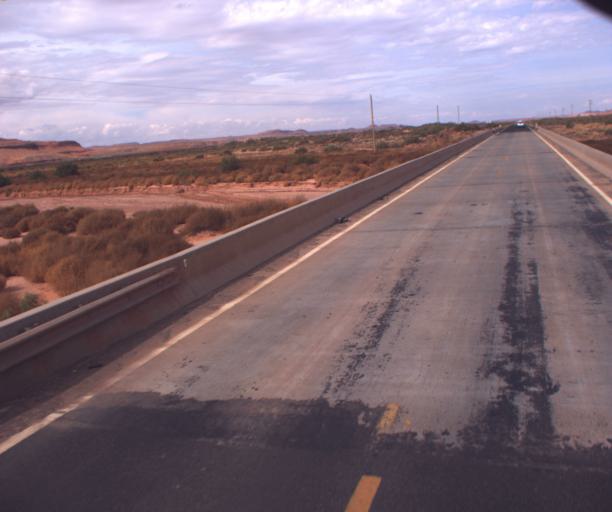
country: US
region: Arizona
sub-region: Apache County
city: Many Farms
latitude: 36.6263
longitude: -109.5835
